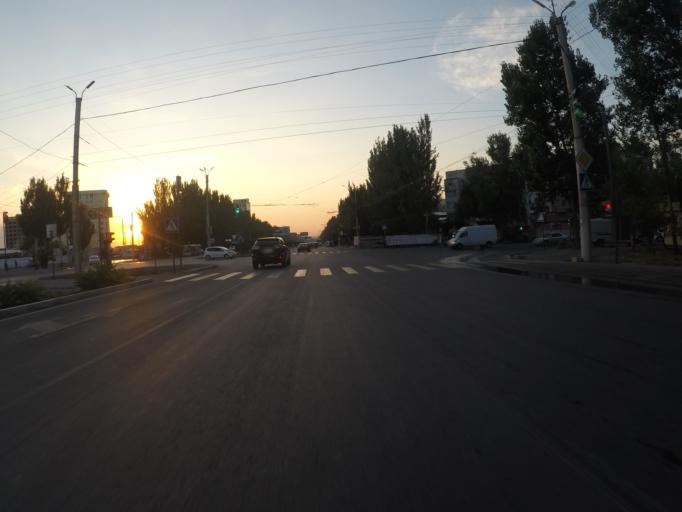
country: KG
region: Chuy
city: Bishkek
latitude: 42.8134
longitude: 74.6311
